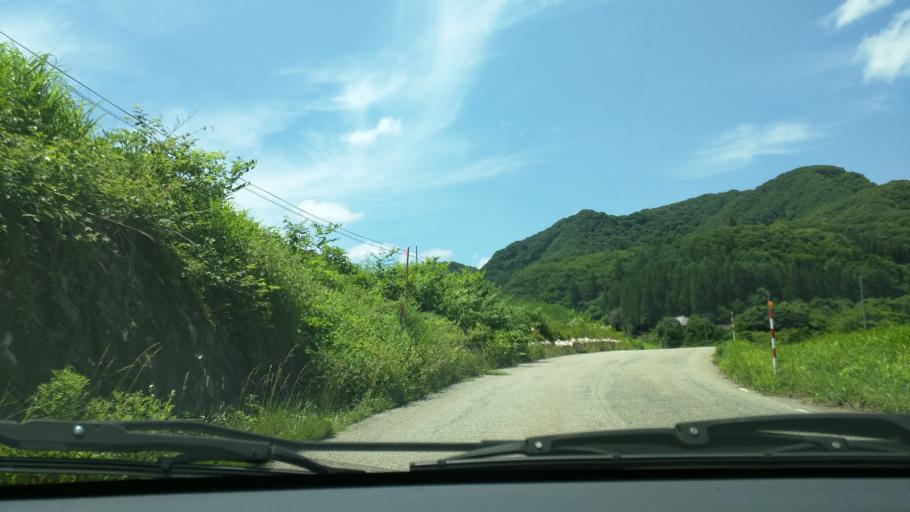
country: JP
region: Fukushima
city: Kitakata
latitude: 37.2567
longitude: 139.7651
